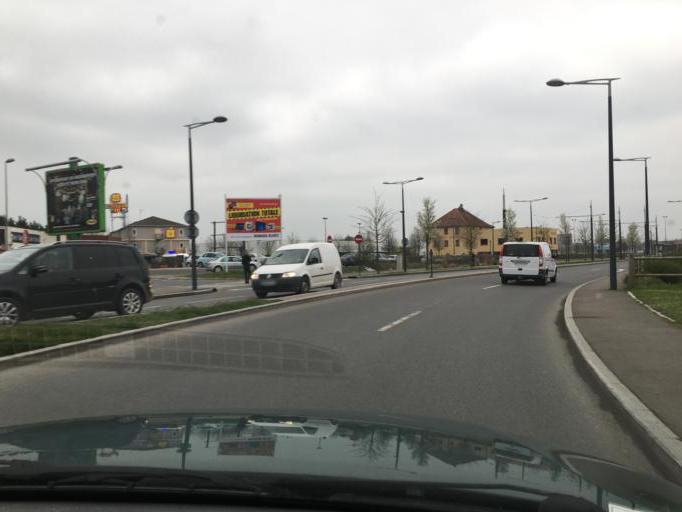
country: FR
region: Centre
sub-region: Departement du Loiret
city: Saint-Jean-de-la-Ruelle
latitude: 47.8955
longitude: 1.8543
